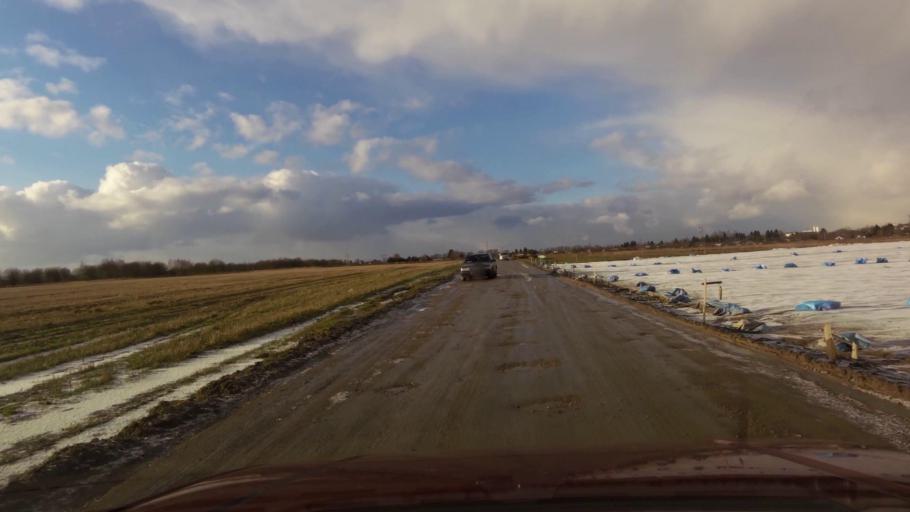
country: PL
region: West Pomeranian Voivodeship
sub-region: Koszalin
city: Koszalin
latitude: 54.1647
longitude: 16.1739
